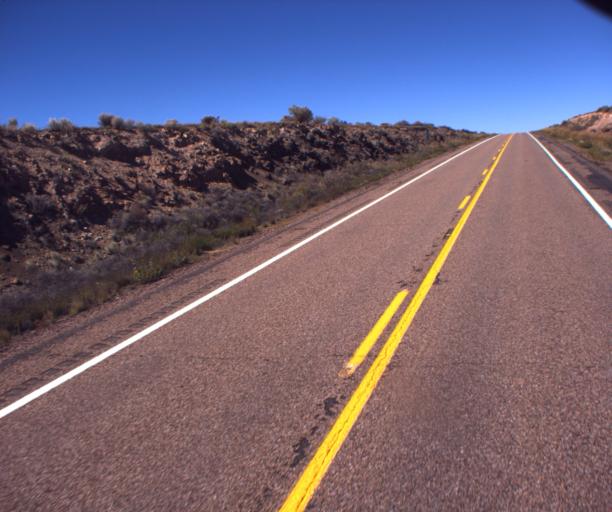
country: US
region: Arizona
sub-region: Apache County
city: Saint Johns
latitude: 34.5579
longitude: -109.4966
